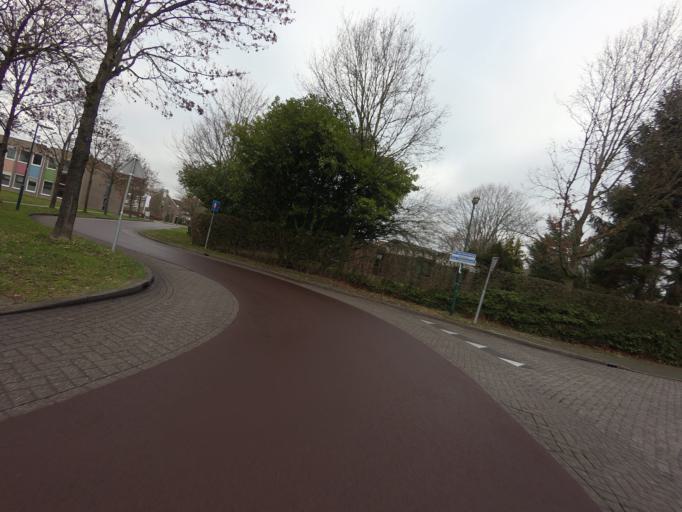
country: NL
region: Utrecht
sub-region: Gemeente Houten
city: Houten
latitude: 52.0242
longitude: 5.1646
